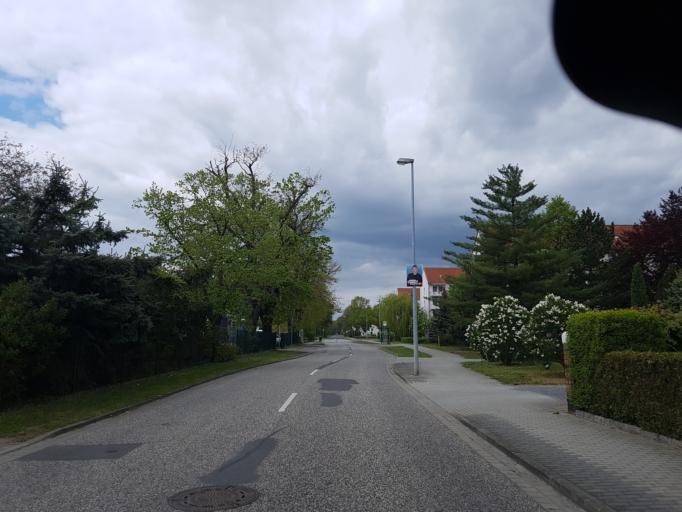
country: DE
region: Brandenburg
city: Altdobern
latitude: 51.6479
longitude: 14.0210
